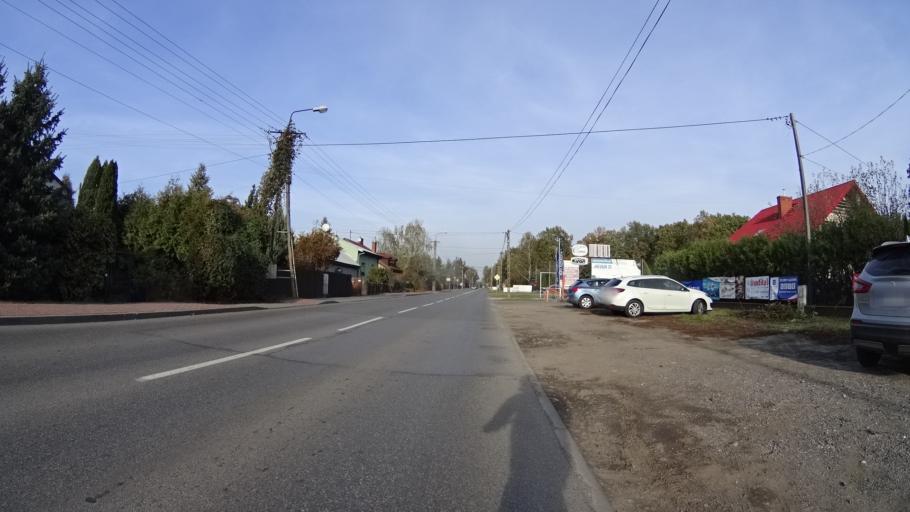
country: PL
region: Masovian Voivodeship
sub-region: Powiat warszawski zachodni
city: Babice
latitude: 52.2535
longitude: 20.8478
